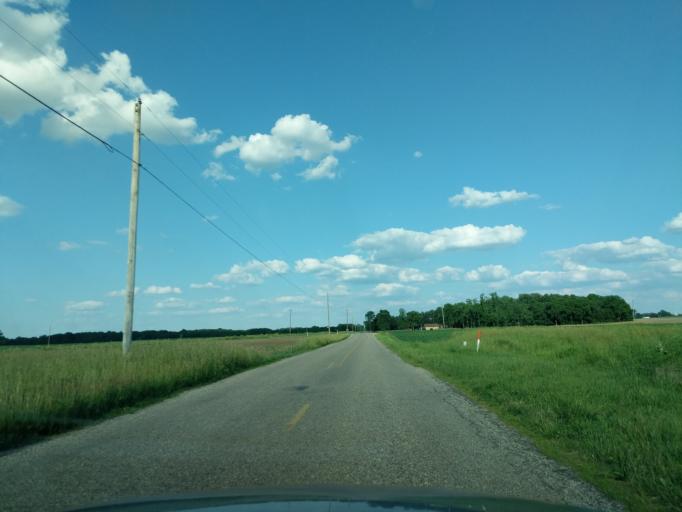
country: US
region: Indiana
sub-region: Kosciusko County
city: North Webster
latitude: 41.3024
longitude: -85.6160
